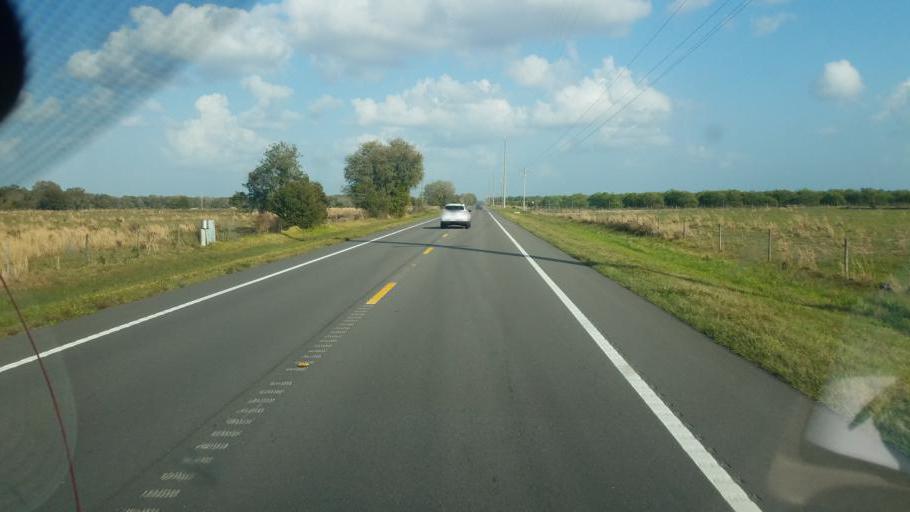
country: US
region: Florida
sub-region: Hardee County
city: Wauchula
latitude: 27.4851
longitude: -81.9951
